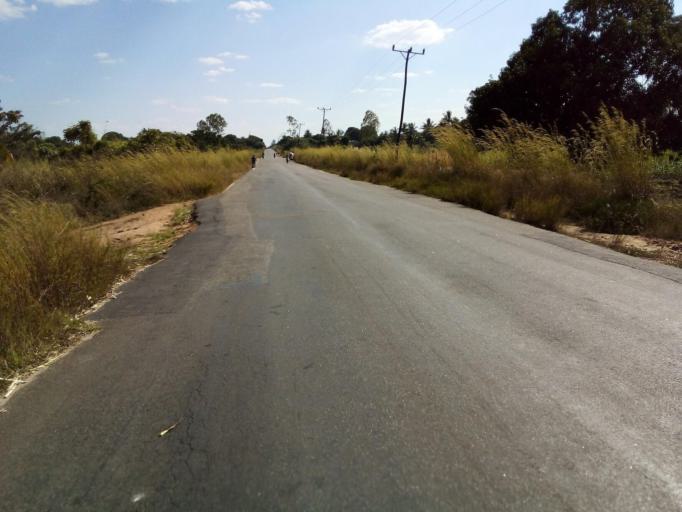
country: MZ
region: Zambezia
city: Quelimane
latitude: -17.5777
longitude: 36.6767
